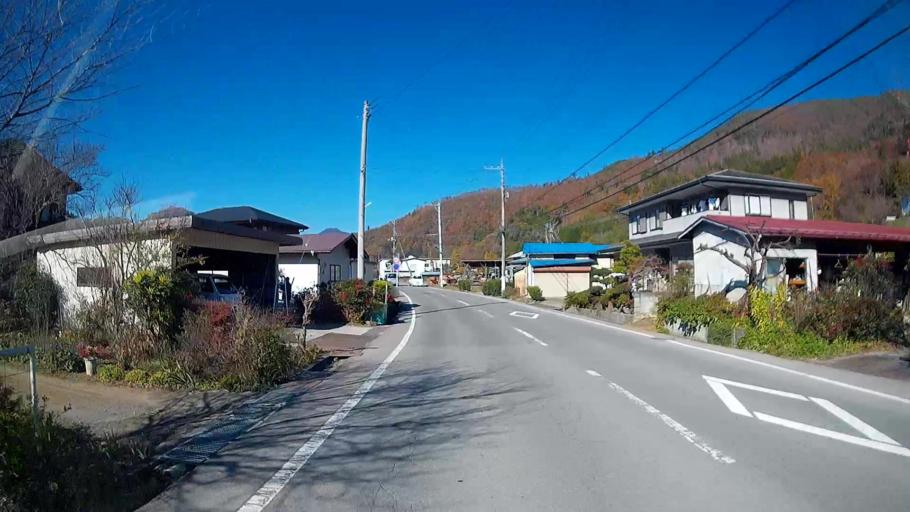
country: JP
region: Yamanashi
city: Otsuki
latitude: 35.5611
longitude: 138.9464
